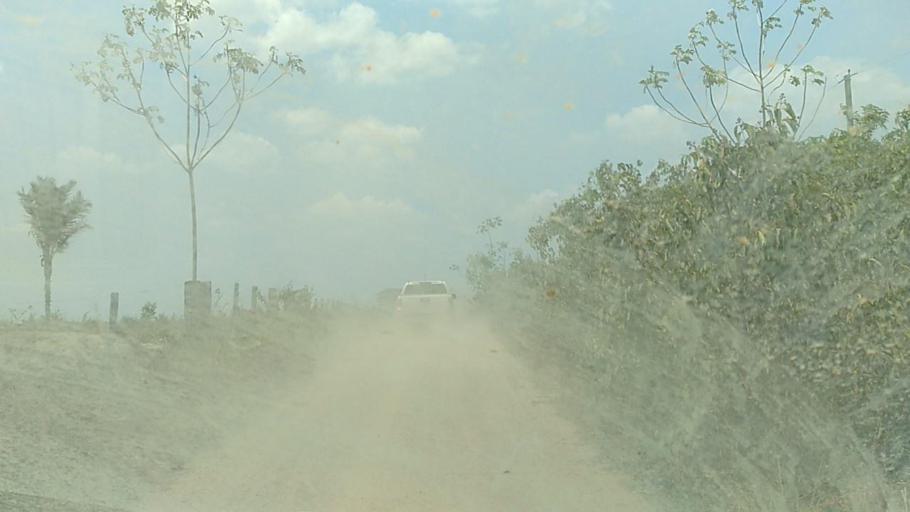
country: BR
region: Rondonia
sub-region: Porto Velho
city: Porto Velho
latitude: -8.7291
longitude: -63.2951
